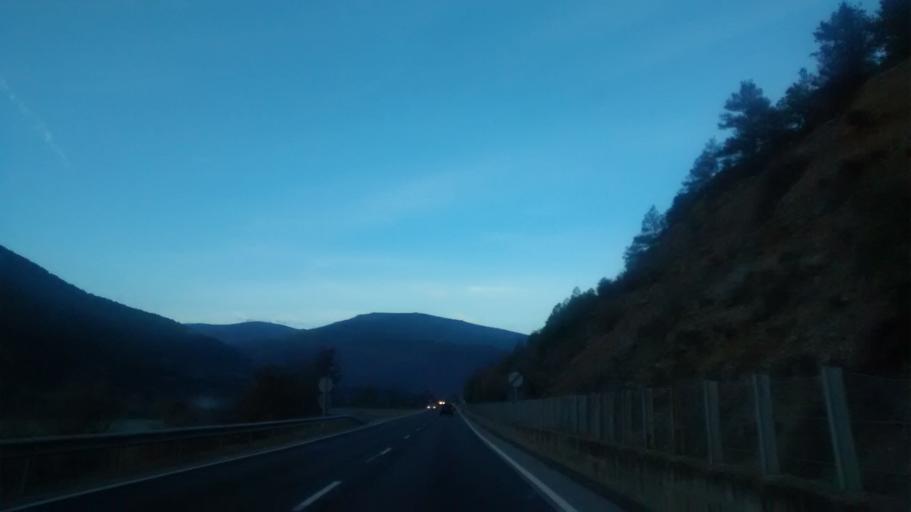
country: ES
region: Catalonia
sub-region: Provincia de Lleida
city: Coll de Nargo
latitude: 42.2712
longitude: 1.3608
